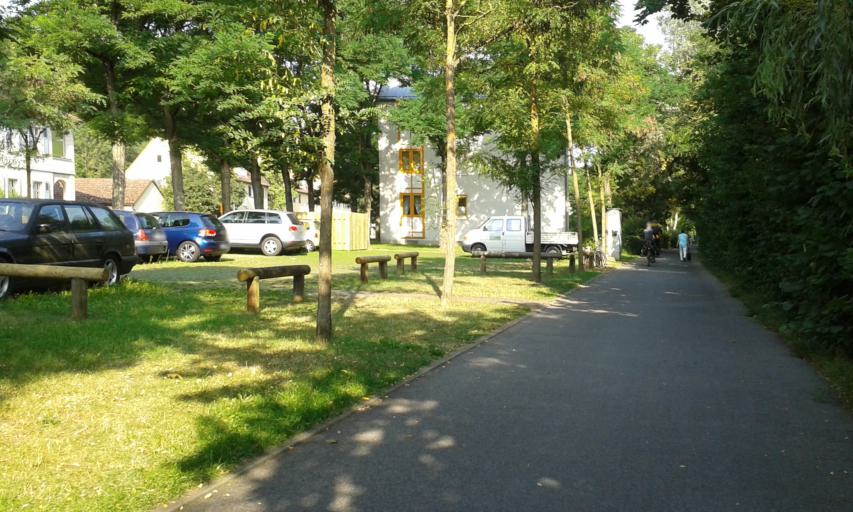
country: DE
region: Bavaria
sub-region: Upper Franconia
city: Hallstadt
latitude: 49.9017
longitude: 10.8689
